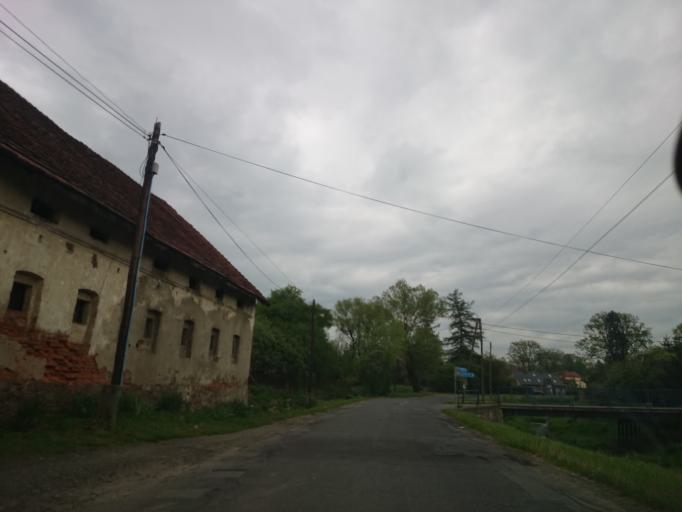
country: PL
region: Lower Silesian Voivodeship
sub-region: Powiat klodzki
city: Klodzko
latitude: 50.4215
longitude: 16.6833
